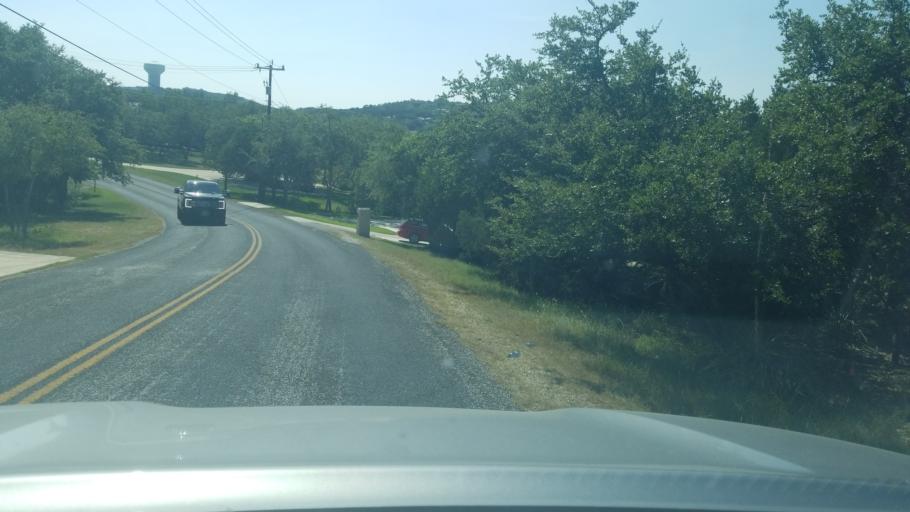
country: US
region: Texas
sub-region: Bexar County
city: Timberwood Park
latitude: 29.6824
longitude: -98.4995
